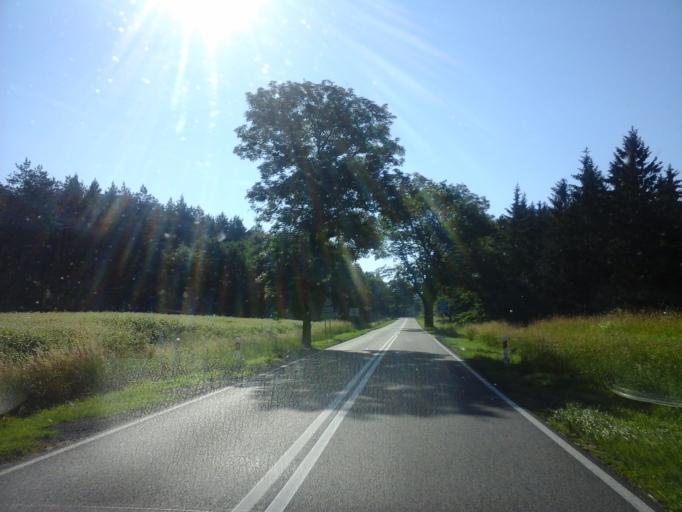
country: PL
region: West Pomeranian Voivodeship
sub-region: Powiat drawski
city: Drawsko Pomorskie
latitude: 53.4959
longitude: 15.6956
